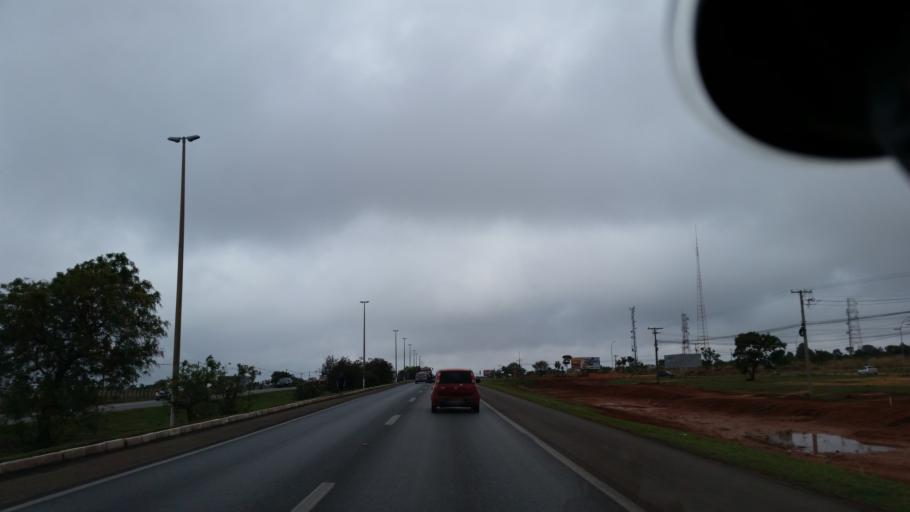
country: BR
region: Goias
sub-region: Luziania
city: Luziania
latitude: -16.0192
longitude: -47.9809
